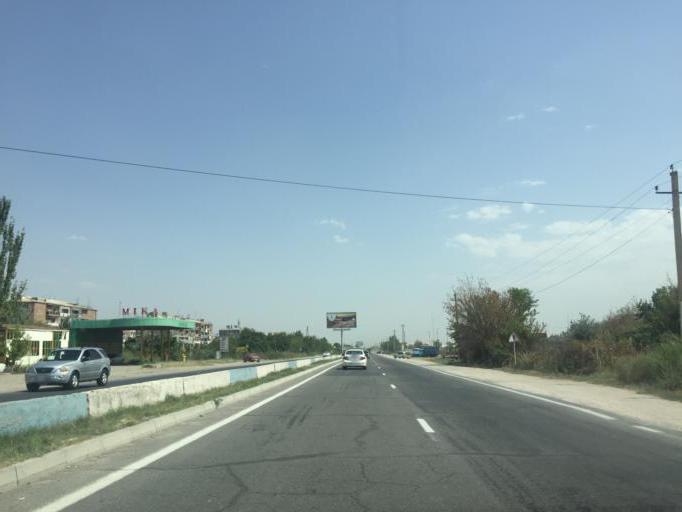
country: AM
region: Ararat
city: Artashat
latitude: 39.9508
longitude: 44.5421
